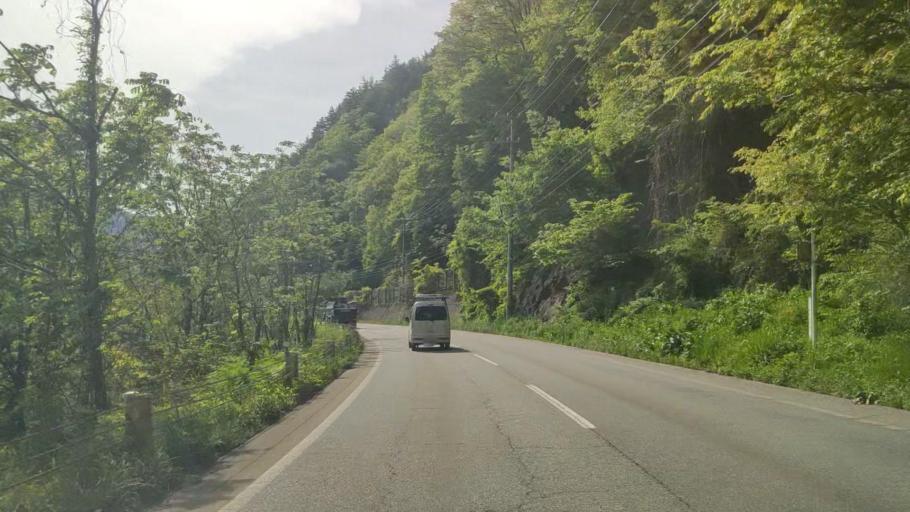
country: JP
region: Gifu
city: Takayama
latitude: 36.2589
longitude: 137.4670
